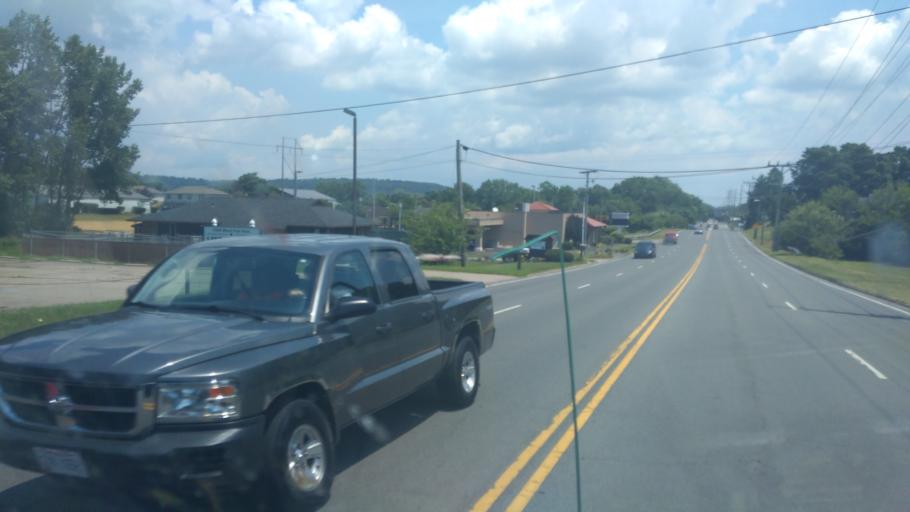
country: US
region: Ohio
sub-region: Fairfield County
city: Lancaster
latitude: 39.7253
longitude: -82.6335
